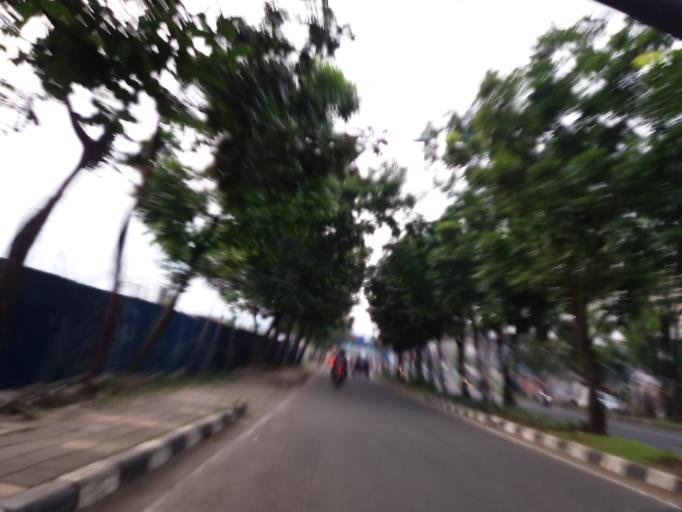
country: ID
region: West Java
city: Bandung
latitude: -6.9155
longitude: 107.6438
